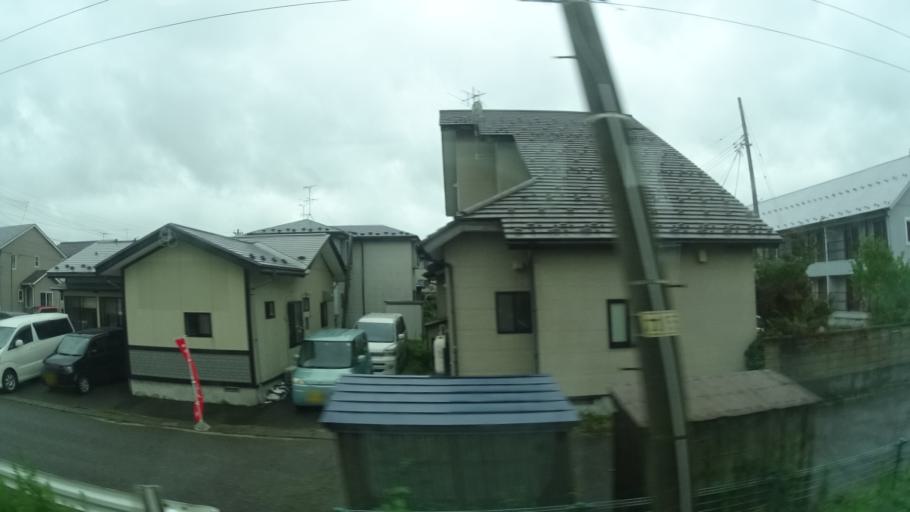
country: JP
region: Yamagata
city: Tsuruoka
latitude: 38.7414
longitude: 139.8076
